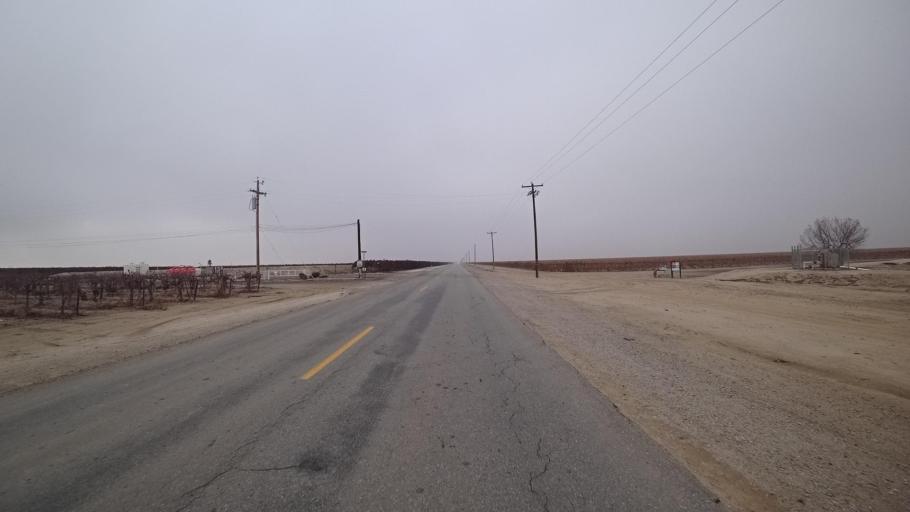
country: US
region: California
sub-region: Kern County
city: Greenfield
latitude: 35.0943
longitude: -119.1537
